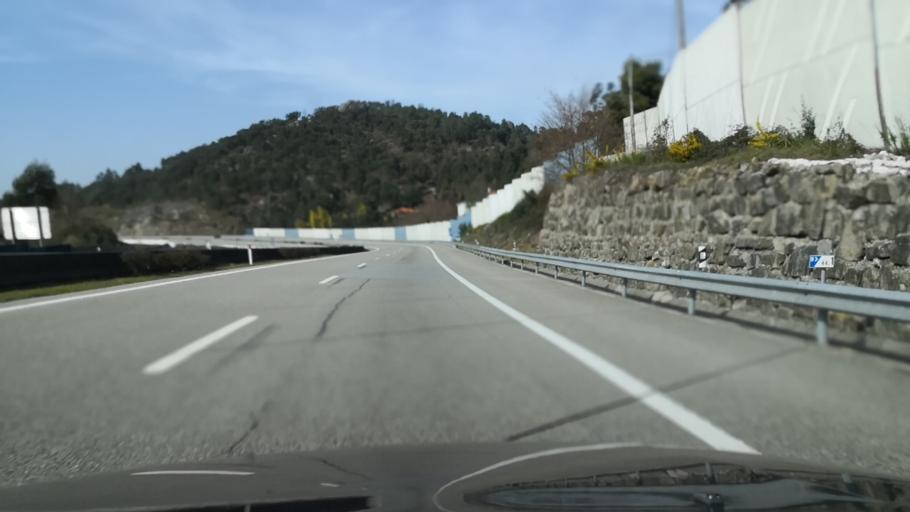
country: PT
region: Aveiro
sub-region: Sever do Vouga
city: Sever do Vouga
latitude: 40.6674
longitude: -8.3277
